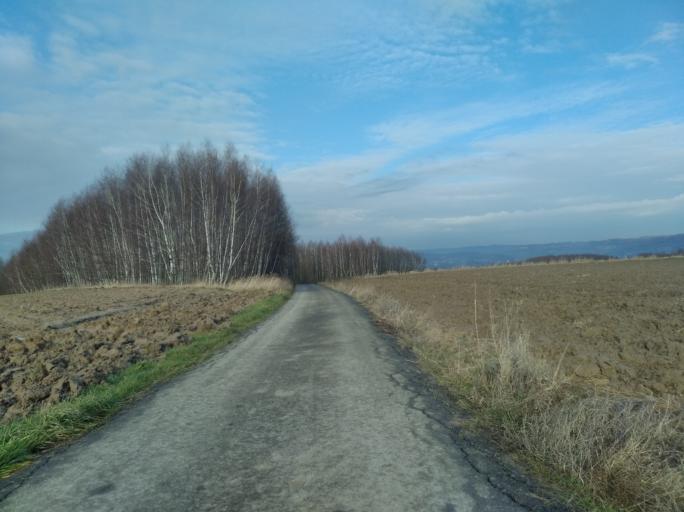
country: PL
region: Subcarpathian Voivodeship
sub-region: Powiat strzyzowski
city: Wysoka Strzyzowska
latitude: 49.8508
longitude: 21.7453
